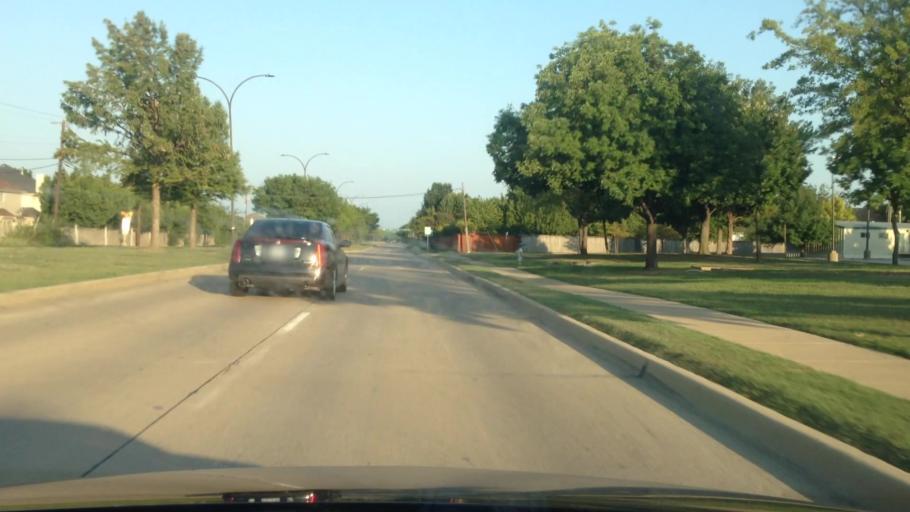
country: US
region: Texas
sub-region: Tarrant County
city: Dalworthington Gardens
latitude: 32.6562
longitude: -97.1035
